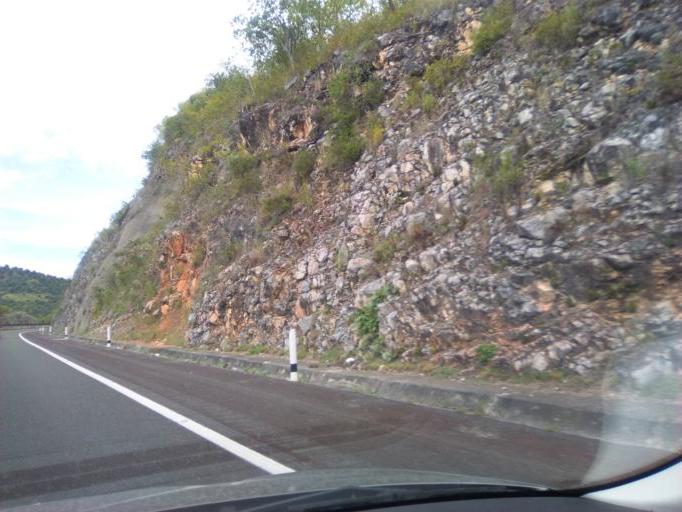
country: MX
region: Guerrero
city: Huitziltepec
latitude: 17.7296
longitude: -99.5011
